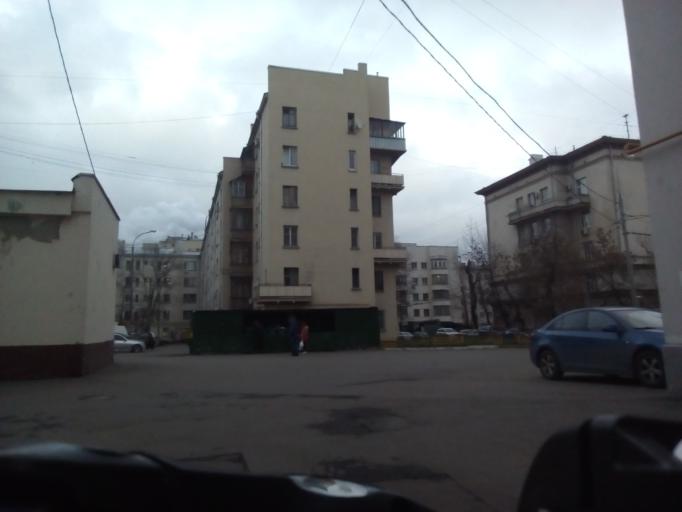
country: RU
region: Moscow
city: Lefortovo
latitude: 55.7494
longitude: 37.7159
